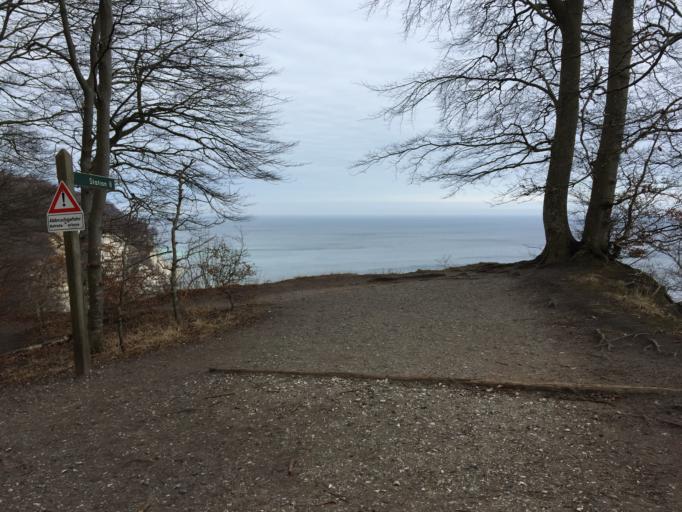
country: DE
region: Mecklenburg-Vorpommern
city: Sassnitz
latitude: 54.5362
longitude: 13.6778
